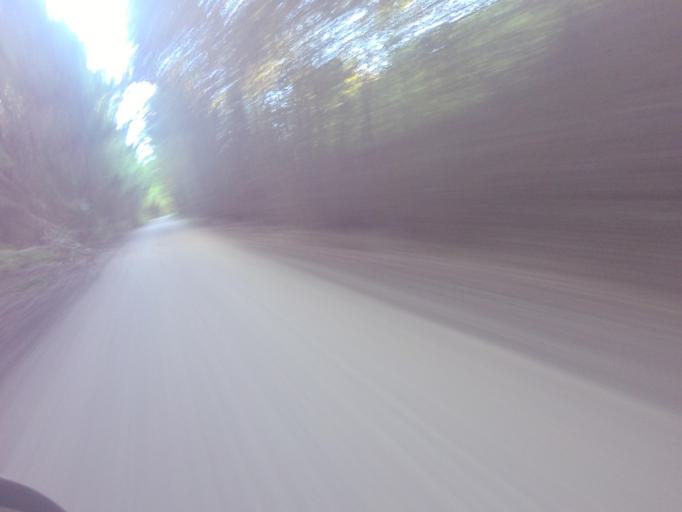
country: CA
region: Ontario
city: Bradford West Gwillimbury
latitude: 44.0048
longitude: -79.8098
